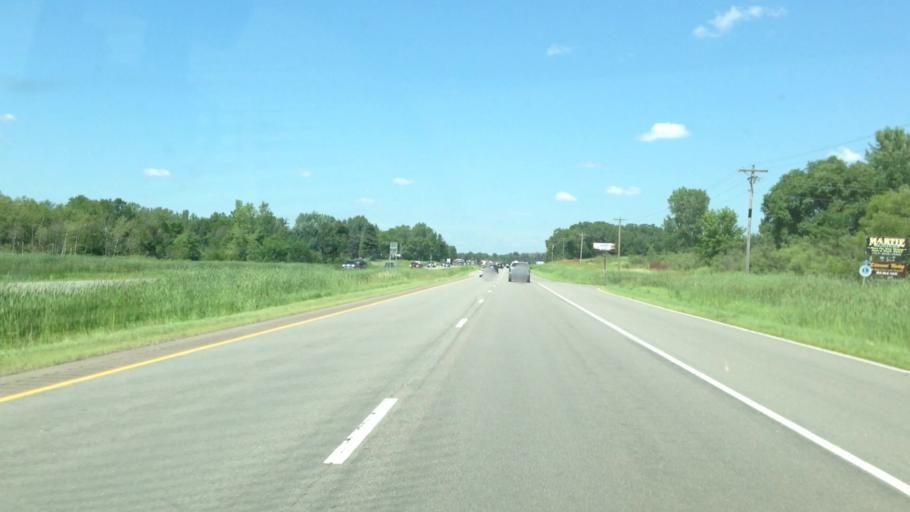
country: US
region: Minnesota
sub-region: Sherburne County
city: Zimmerman
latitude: 45.4304
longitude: -93.5749
